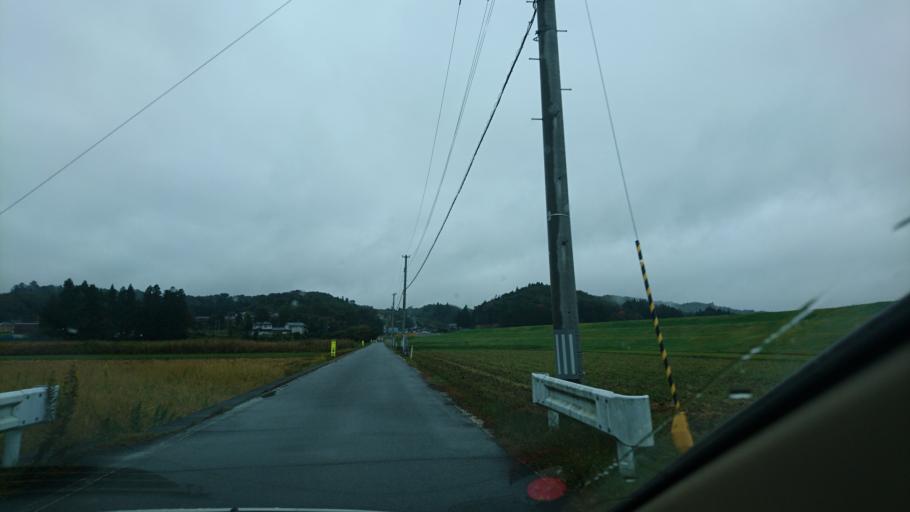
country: JP
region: Iwate
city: Ichinoseki
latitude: 38.9779
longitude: 141.1102
